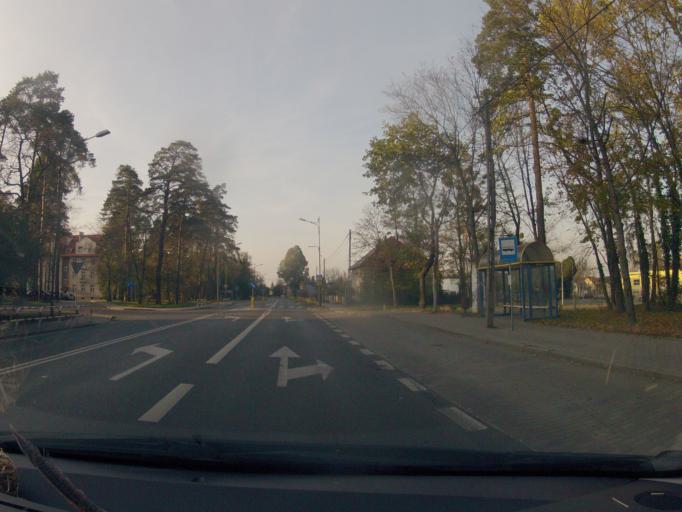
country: PL
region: Opole Voivodeship
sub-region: Powiat strzelecki
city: Strzelce Opolskie
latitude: 50.5174
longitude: 18.2874
